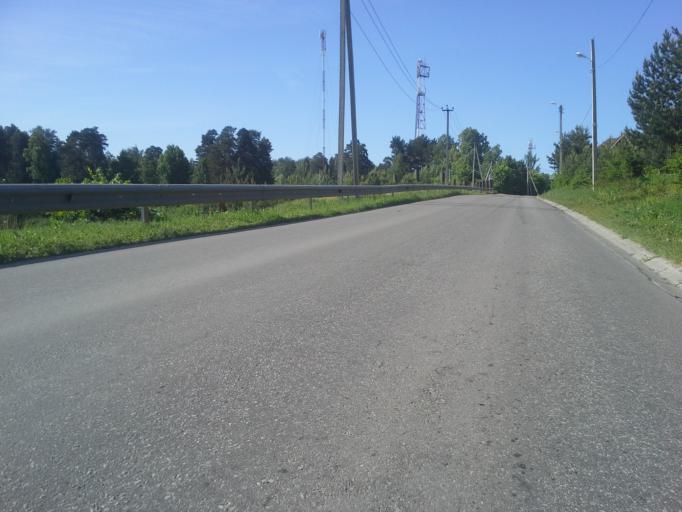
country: RU
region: Moskovskaya
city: Vatutinki
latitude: 55.4502
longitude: 37.3985
